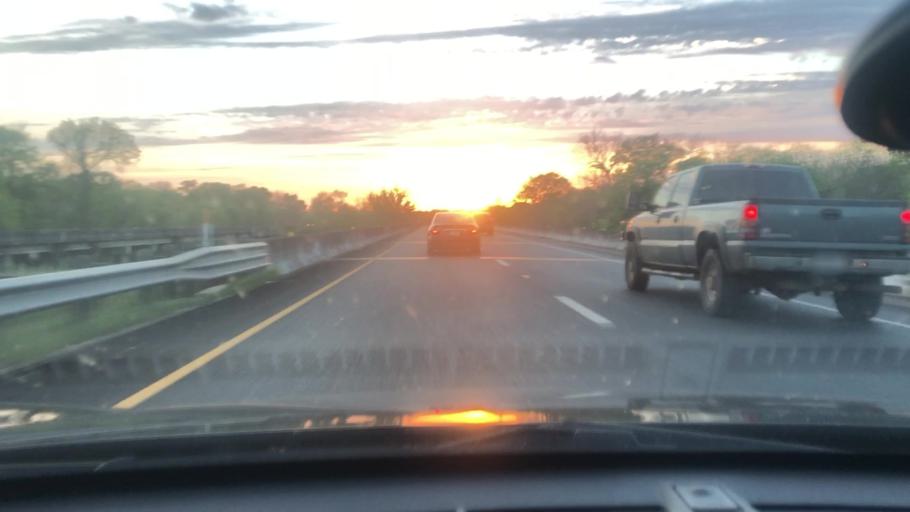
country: US
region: Texas
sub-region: Jackson County
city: Edna
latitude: 28.9602
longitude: -96.6852
